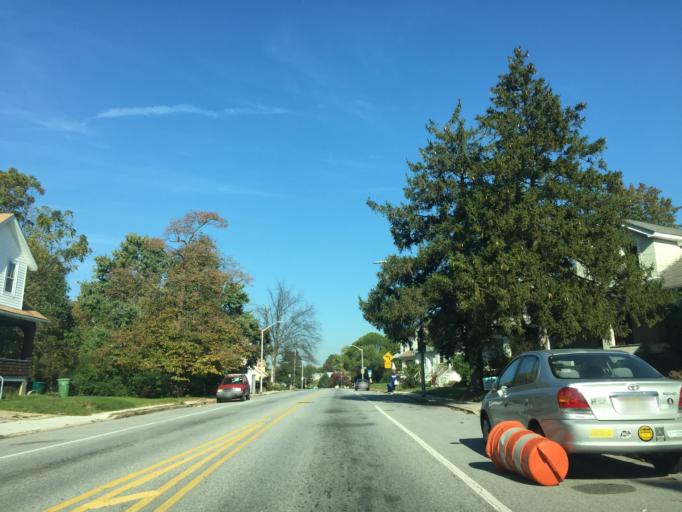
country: US
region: Maryland
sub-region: Baltimore County
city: Parkville
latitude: 39.3468
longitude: -76.5595
